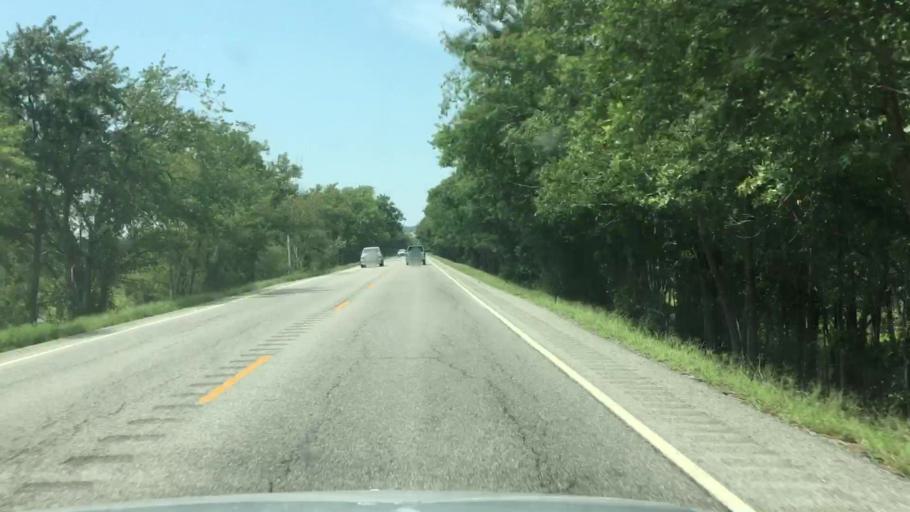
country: US
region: Oklahoma
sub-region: Muskogee County
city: Fort Gibson
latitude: 35.9370
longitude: -95.2141
